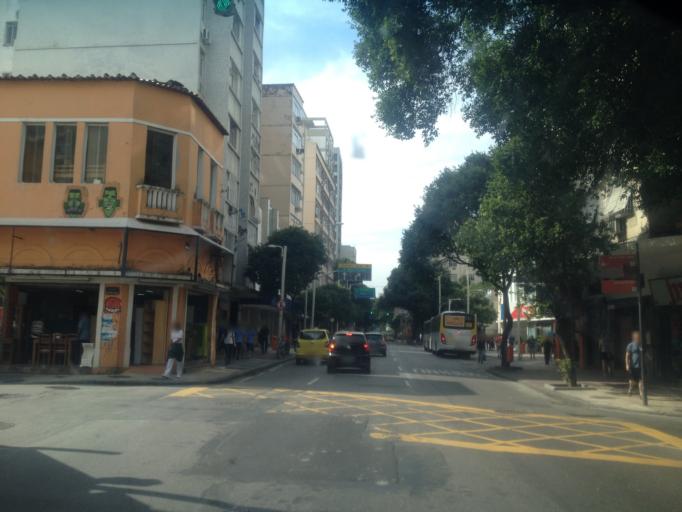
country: BR
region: Rio de Janeiro
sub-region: Rio De Janeiro
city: Rio de Janeiro
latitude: -22.9534
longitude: -43.1899
